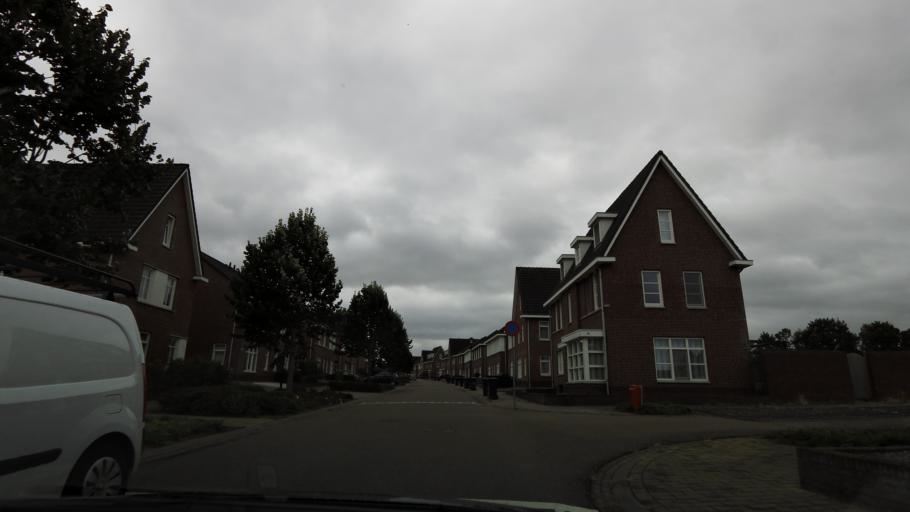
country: NL
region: Limburg
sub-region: Gemeente Heerlen
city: Nieuw-Lotbroek
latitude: 50.9117
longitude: 5.9219
